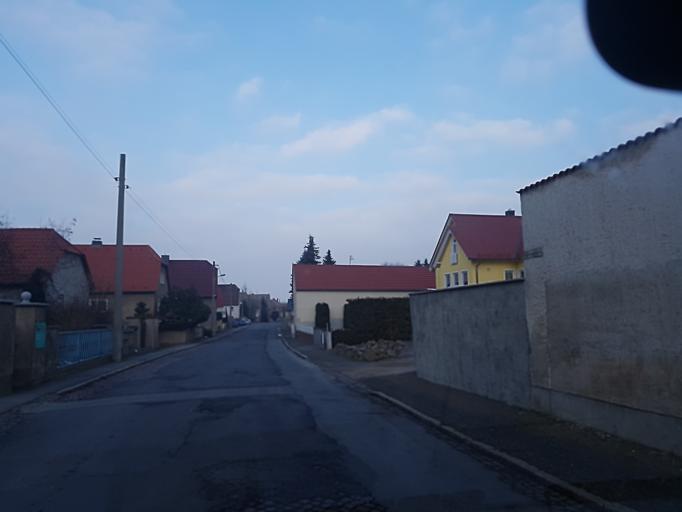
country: DE
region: Saxony
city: Oschatz
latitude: 51.3206
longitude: 13.0865
